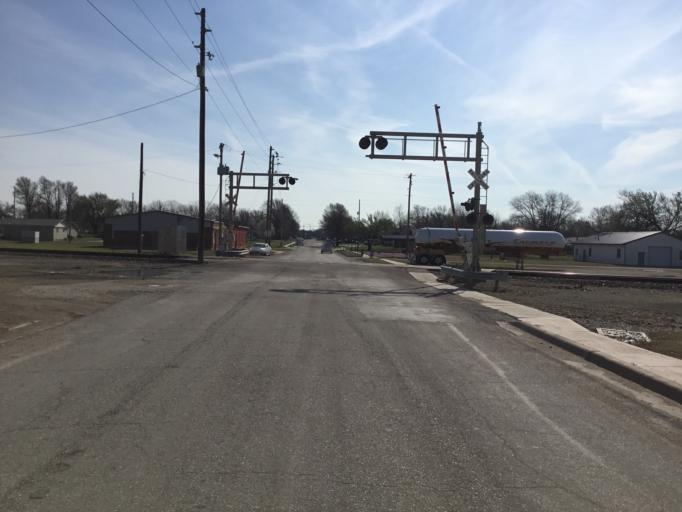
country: US
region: Kansas
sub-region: Butler County
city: Douglass
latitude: 37.5174
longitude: -97.0102
